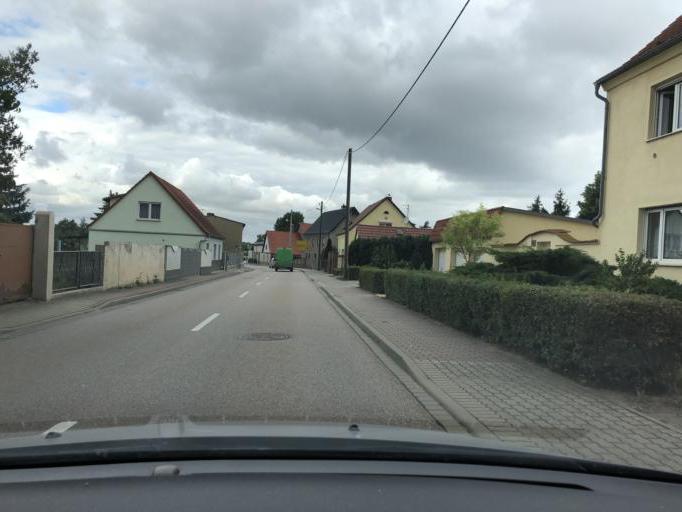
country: DE
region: Saxony-Anhalt
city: Lochau
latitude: 51.3985
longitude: 12.0526
